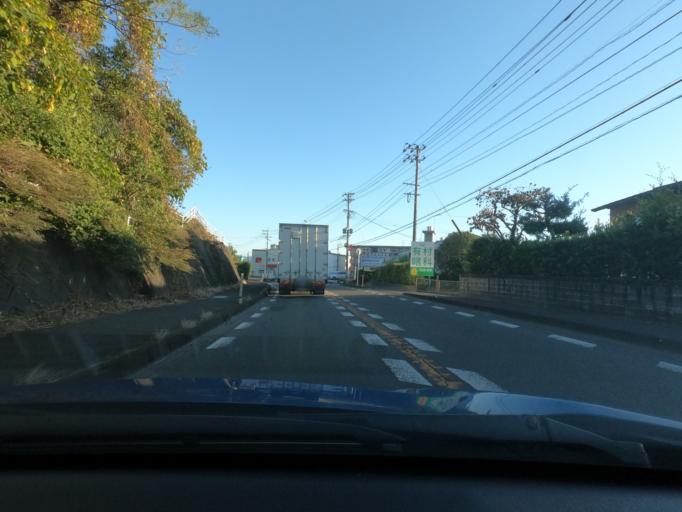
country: JP
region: Kagoshima
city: Satsumasendai
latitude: 31.8391
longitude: 130.2834
